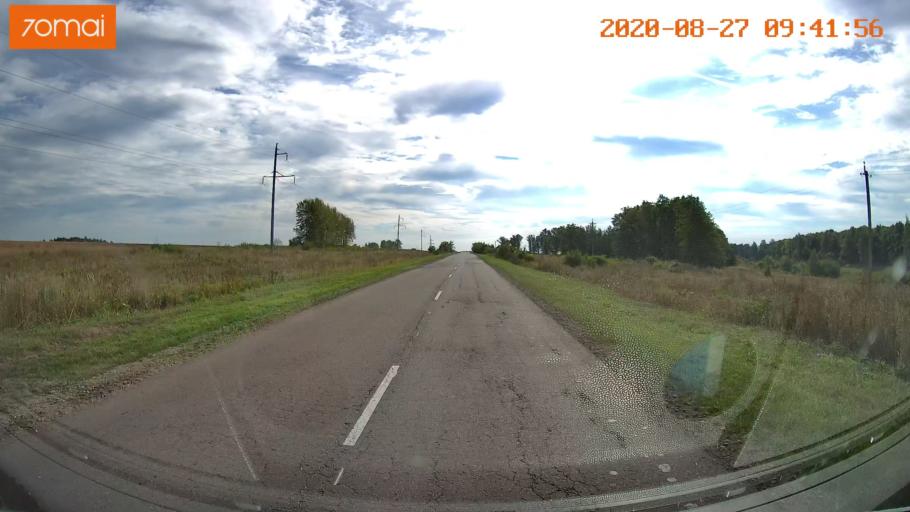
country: RU
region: Tula
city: Kurkino
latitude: 53.3760
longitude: 38.4301
